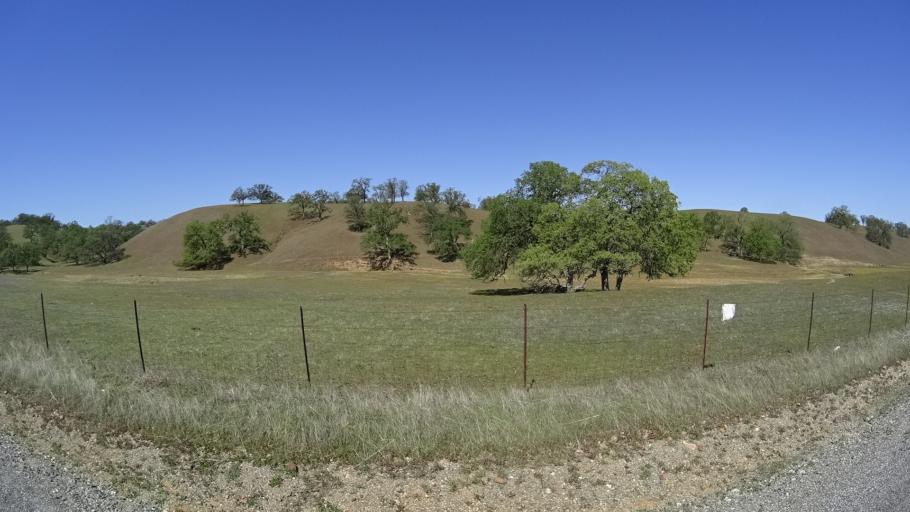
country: US
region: California
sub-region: Glenn County
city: Orland
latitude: 39.7479
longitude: -122.3666
